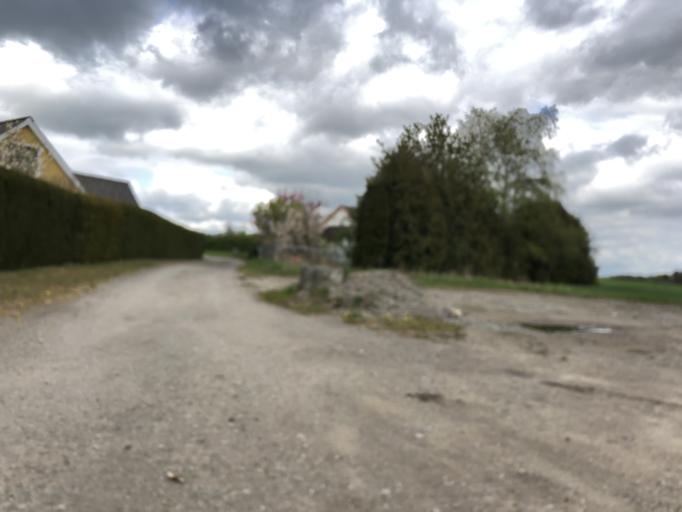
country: SE
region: Skane
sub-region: Lunds Kommun
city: Lund
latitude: 55.7136
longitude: 13.2987
